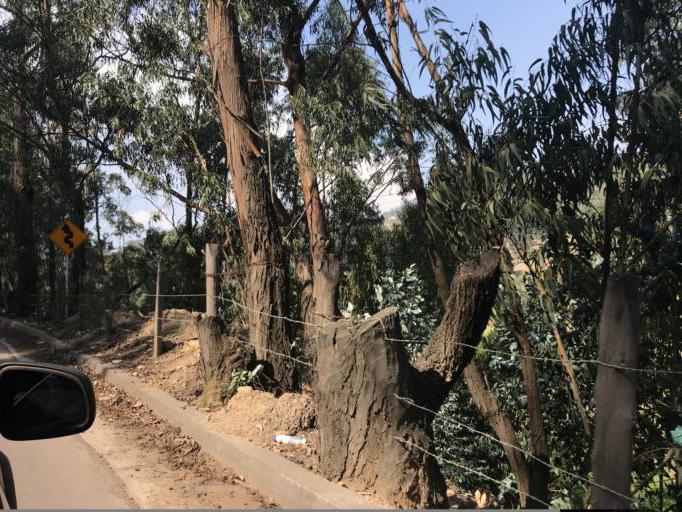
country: CO
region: Boyaca
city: Samaca
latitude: 5.4856
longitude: -73.4781
